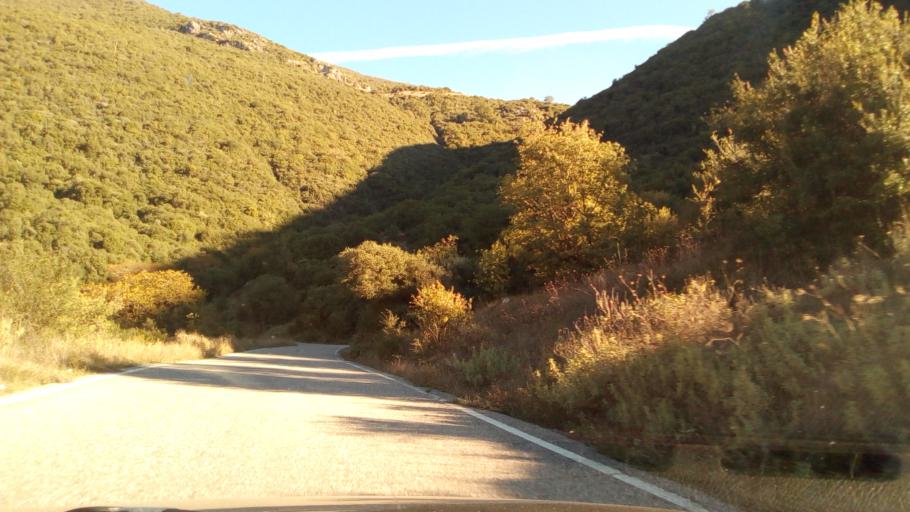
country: GR
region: West Greece
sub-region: Nomos Aitolias kai Akarnanias
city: Nafpaktos
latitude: 38.4785
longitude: 21.8700
